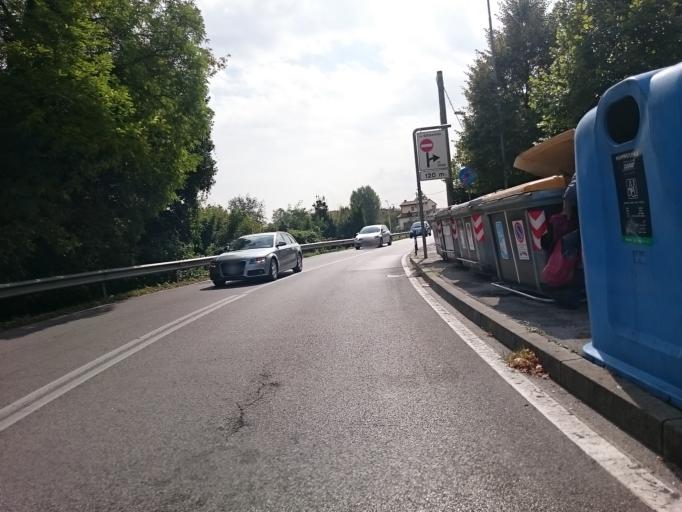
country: IT
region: Veneto
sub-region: Provincia di Padova
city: Padova
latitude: 45.4025
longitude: 11.9014
